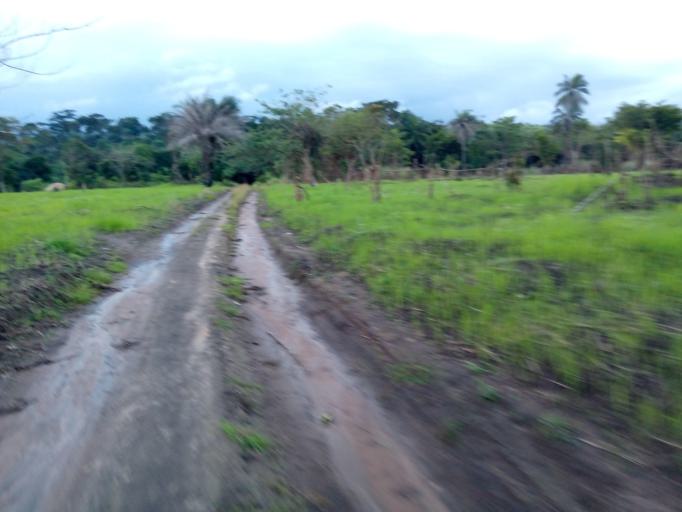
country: SL
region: Eastern Province
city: Buedu
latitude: 8.4919
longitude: -10.3439
